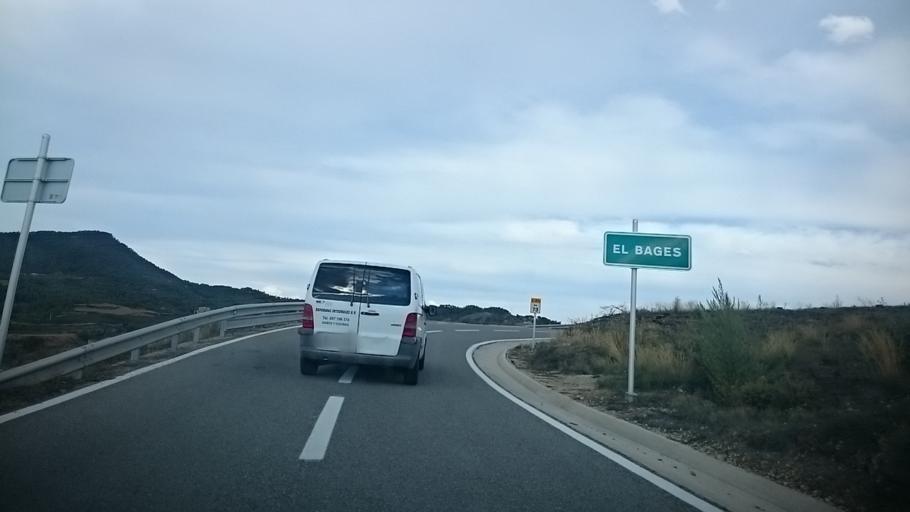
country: ES
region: Catalonia
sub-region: Provincia de Barcelona
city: Odena
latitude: 41.6271
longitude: 1.6732
